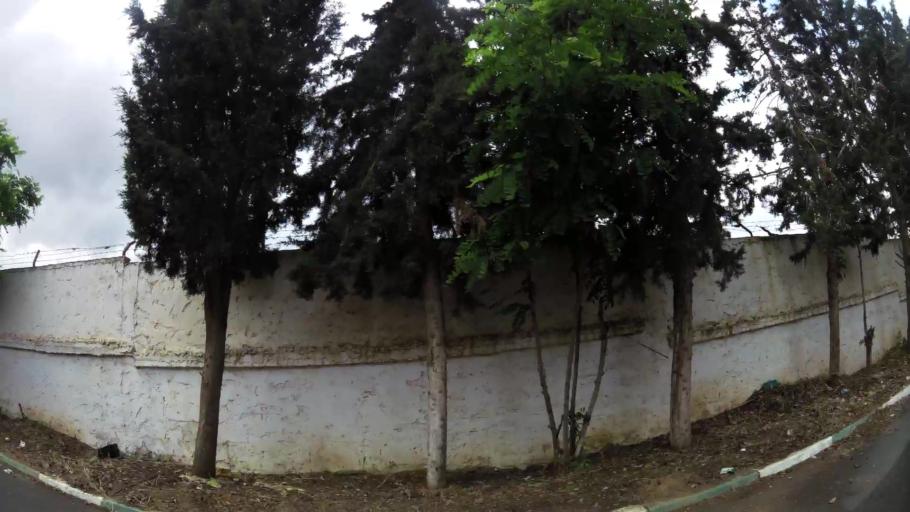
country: MA
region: Rabat-Sale-Zemmour-Zaer
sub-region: Khemisset
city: Tiflet
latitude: 33.8863
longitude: -6.3318
